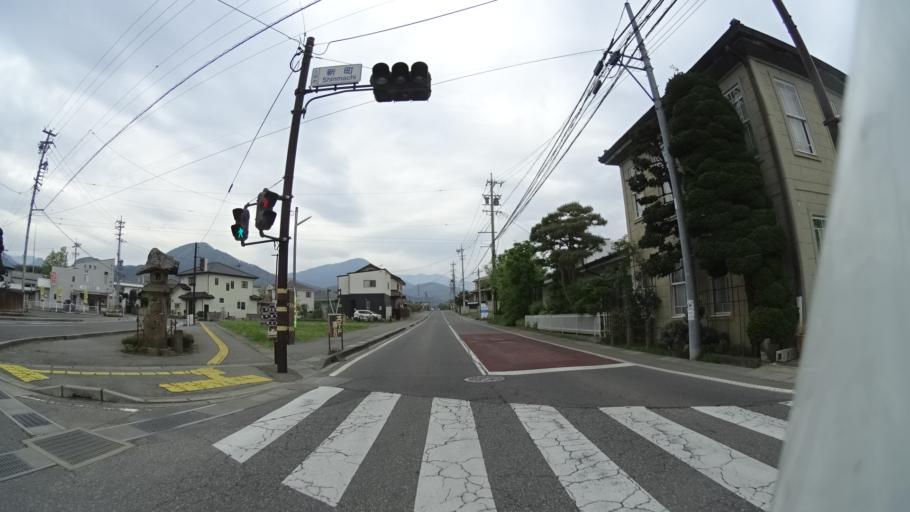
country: JP
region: Nagano
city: Kamimaruko
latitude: 36.3503
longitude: 138.1906
